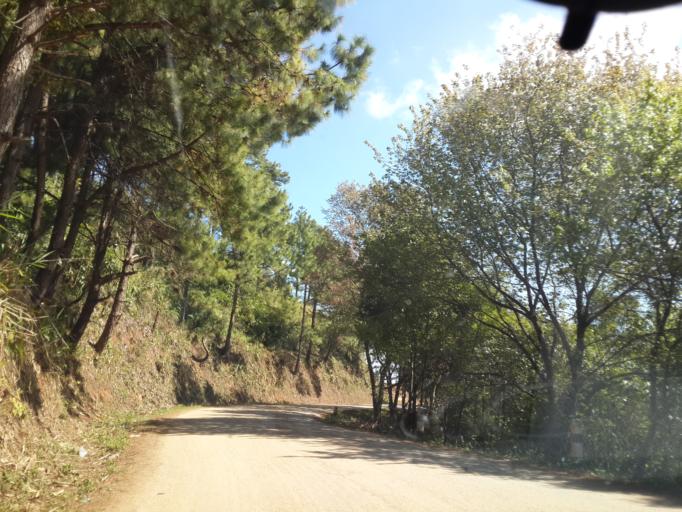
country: TH
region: Chiang Mai
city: Fang
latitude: 19.9272
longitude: 99.0439
